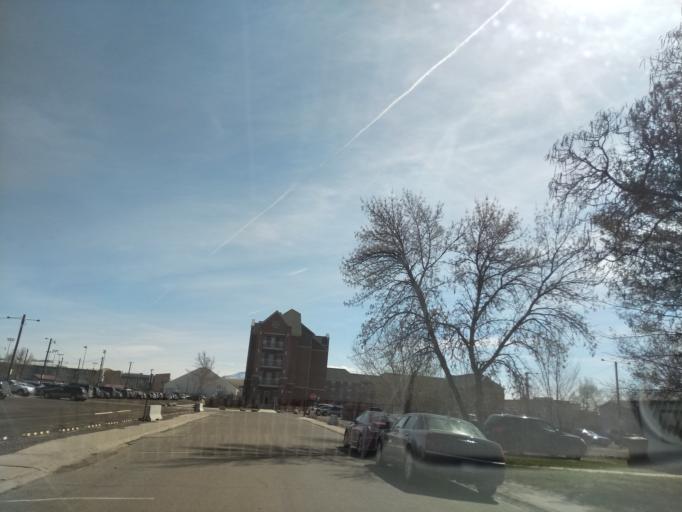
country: US
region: Colorado
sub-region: Mesa County
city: Grand Junction
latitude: 39.0819
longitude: -108.5591
